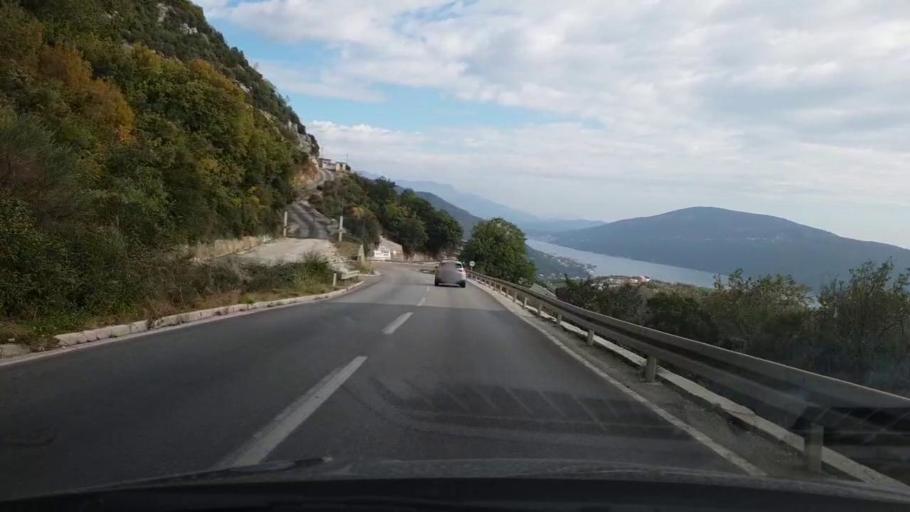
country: ME
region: Herceg Novi
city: Herceg-Novi
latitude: 42.4687
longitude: 18.5413
